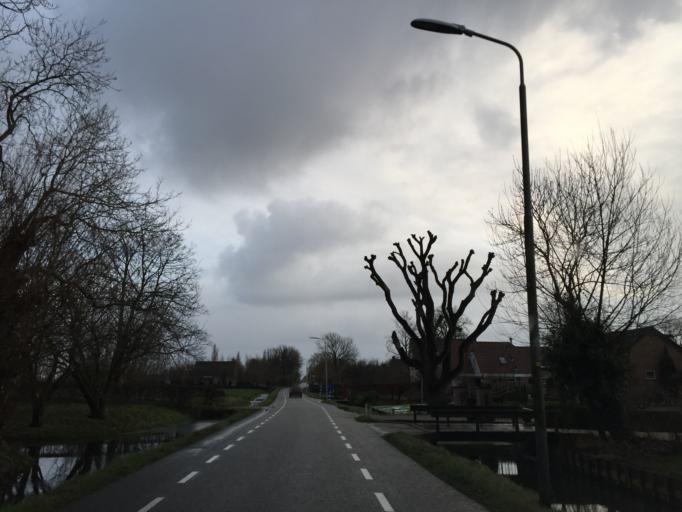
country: NL
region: South Holland
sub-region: Gemeente Pijnacker-Nootdorp
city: Pijnacker
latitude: 52.0048
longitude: 4.3990
